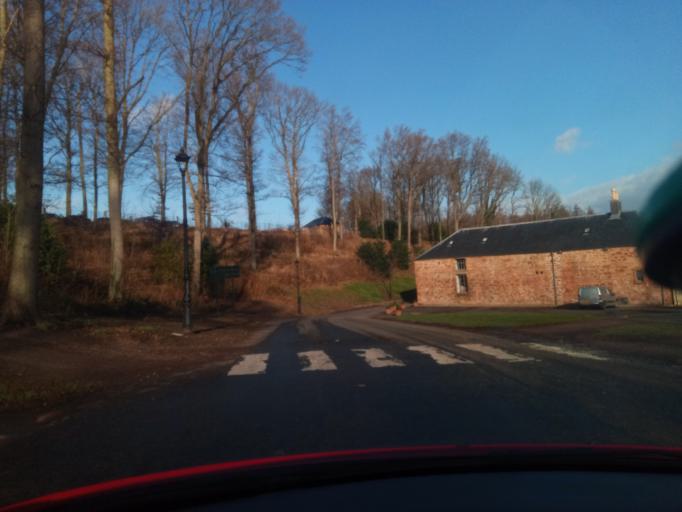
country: GB
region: Scotland
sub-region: Midlothian
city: Dalkeith
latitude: 55.9008
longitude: -3.0617
